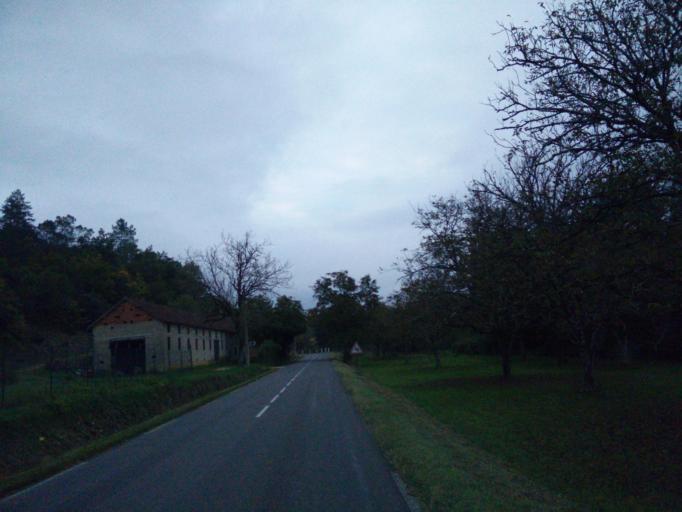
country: FR
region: Aquitaine
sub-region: Departement de la Dordogne
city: Carsac-Aillac
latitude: 44.7924
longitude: 1.3076
